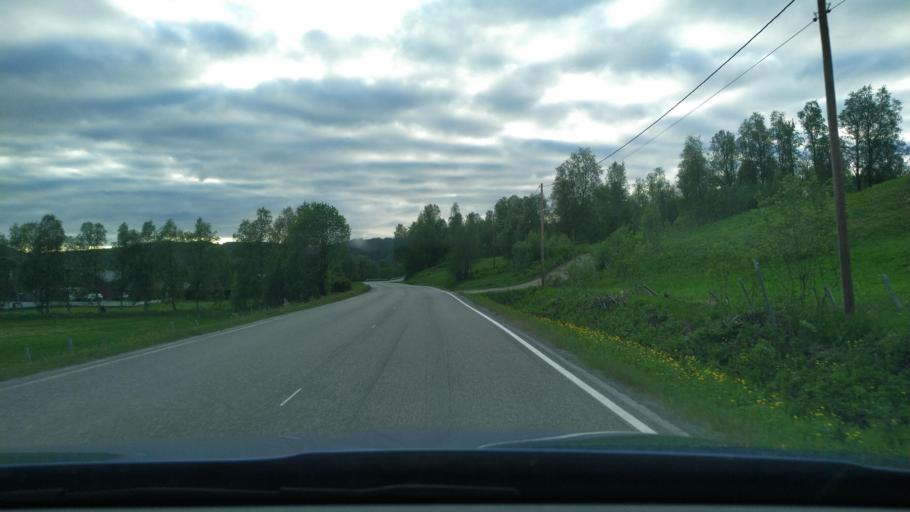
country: NO
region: Troms
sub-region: Sorreisa
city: Sorreisa
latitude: 69.0887
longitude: 18.3518
